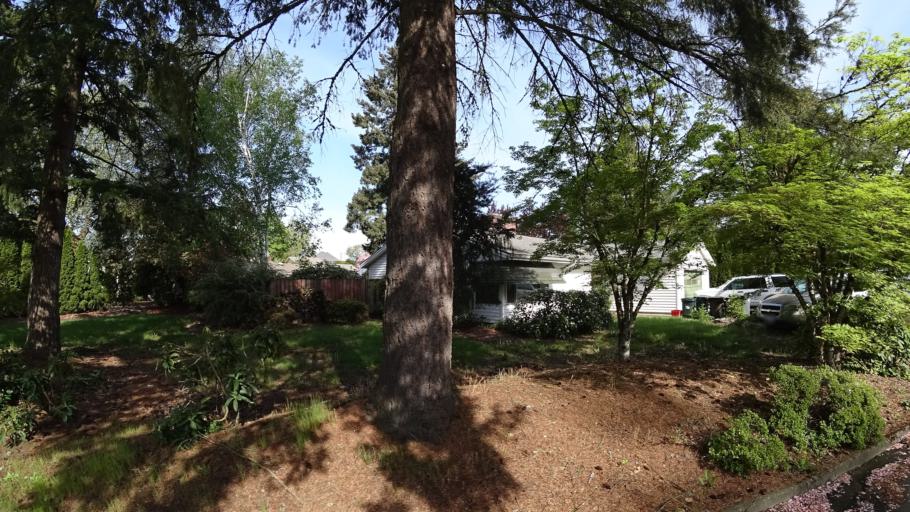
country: US
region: Oregon
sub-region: Washington County
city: Hillsboro
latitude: 45.5233
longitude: -122.9638
